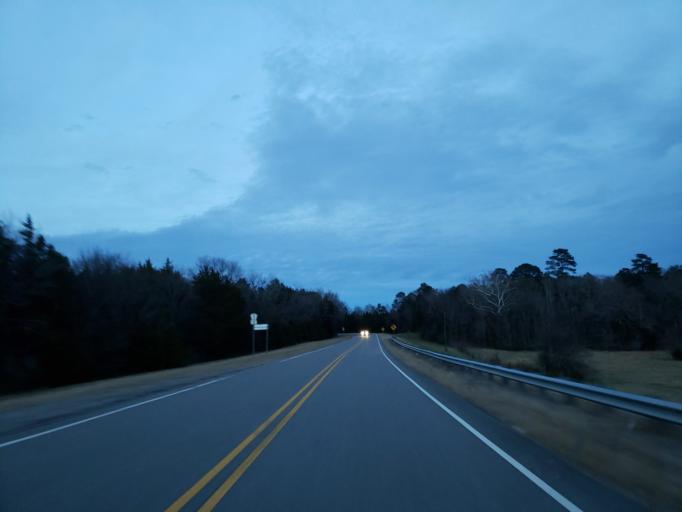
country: US
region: Alabama
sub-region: Greene County
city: Eutaw
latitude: 32.8604
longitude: -88.0975
